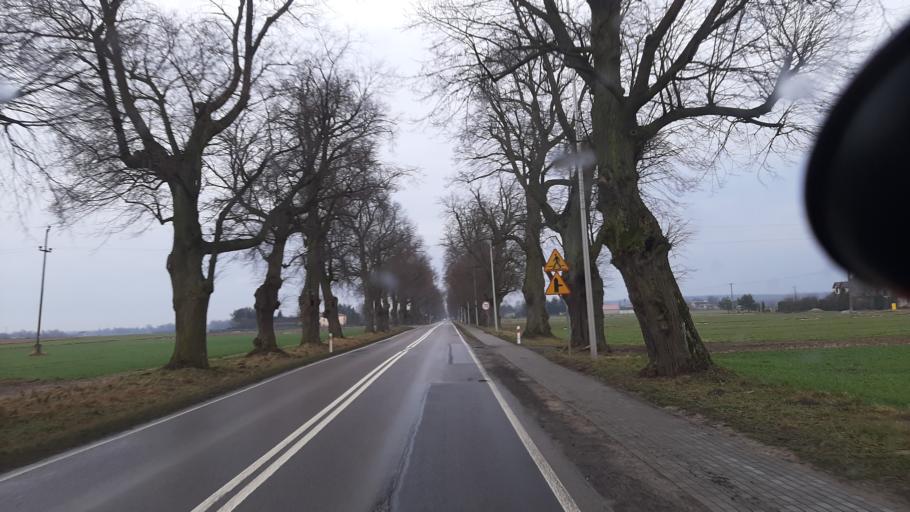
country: PL
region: Lublin Voivodeship
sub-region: Powiat lubelski
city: Jastkow
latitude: 51.3585
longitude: 22.4698
